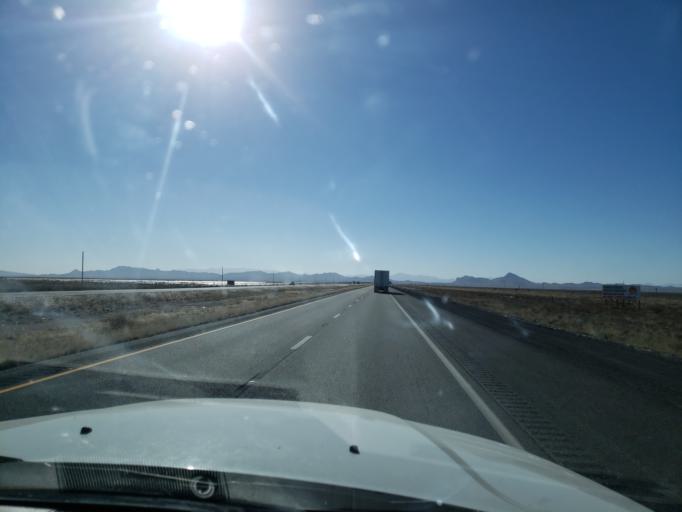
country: US
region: New Mexico
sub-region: Hidalgo County
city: Lordsburg
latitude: 32.2941
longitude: -108.8564
